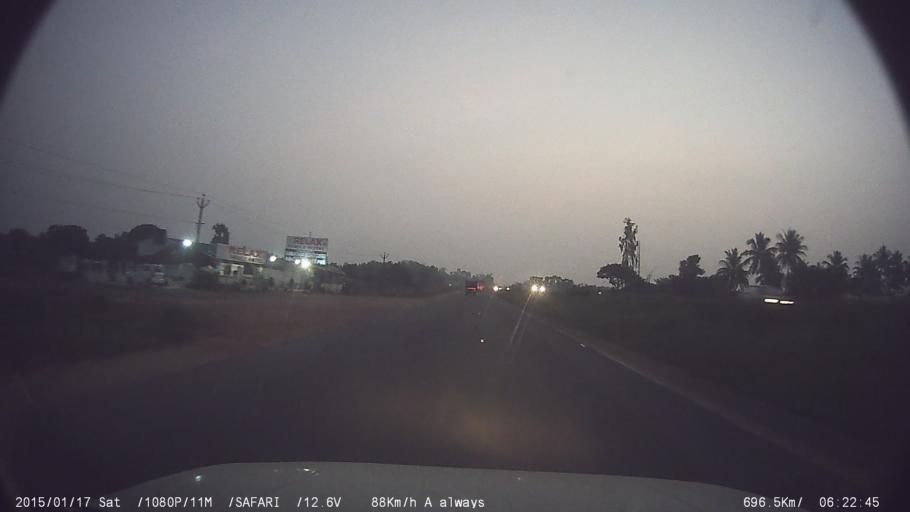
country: IN
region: Tamil Nadu
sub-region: Kancheepuram
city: Sriperumbudur
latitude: 12.9106
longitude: 79.8432
